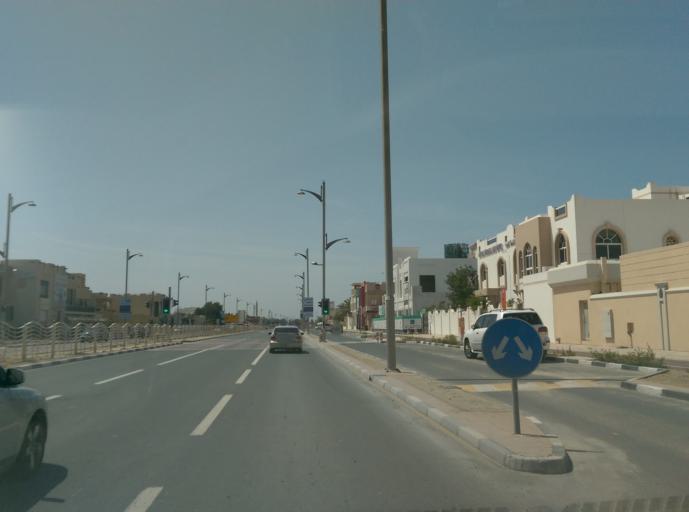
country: AE
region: Dubai
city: Dubai
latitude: 25.1914
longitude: 55.2325
